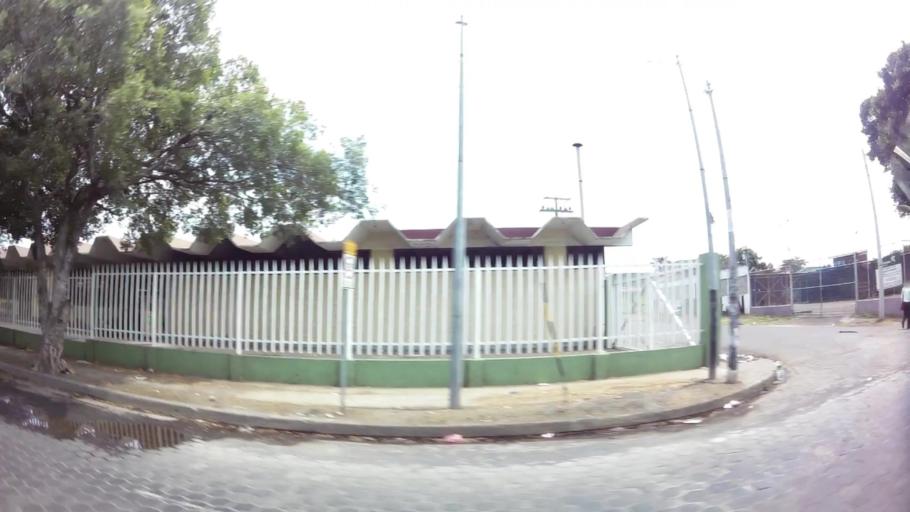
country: NI
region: Managua
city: Managua
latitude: 12.1576
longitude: -86.2905
